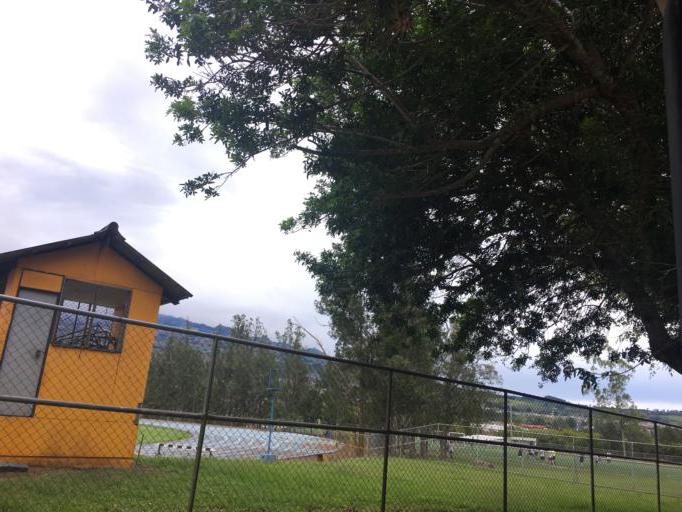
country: CR
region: Cartago
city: Cartago
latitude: 9.8554
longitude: -83.9091
